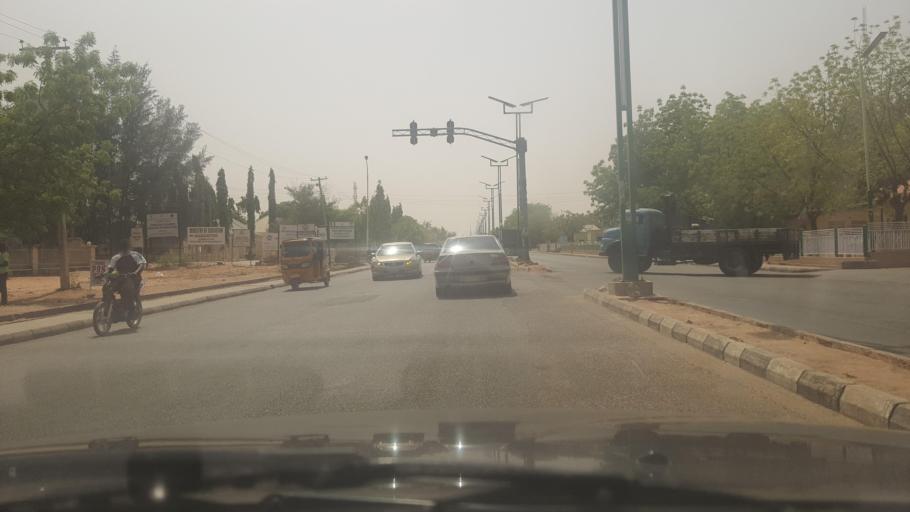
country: NG
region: Gombe
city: Gombe
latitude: 10.2839
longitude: 11.1509
